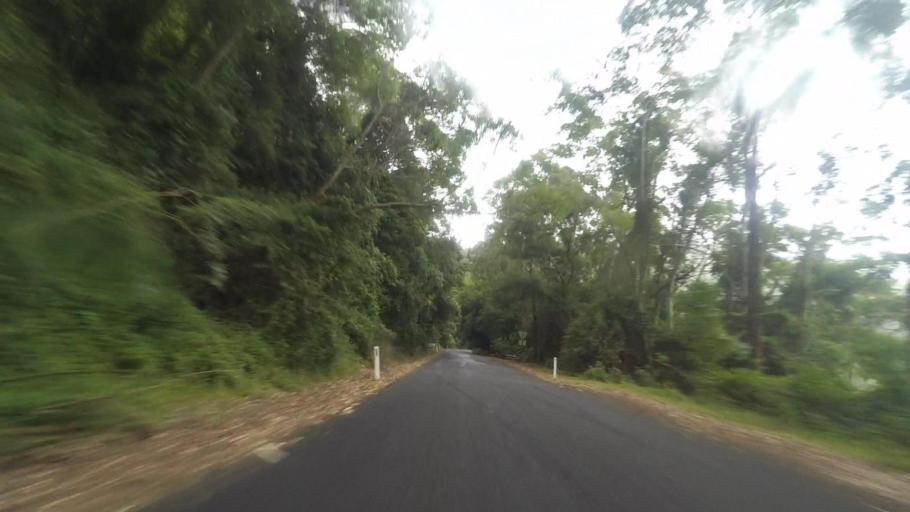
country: AU
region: New South Wales
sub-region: Wollongong
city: Cordeaux Heights
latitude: -34.4165
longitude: 150.8175
